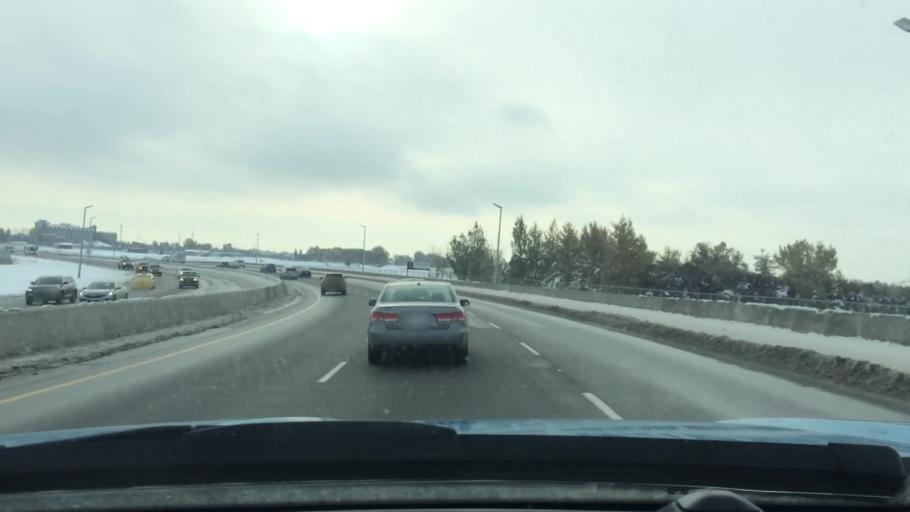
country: CA
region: Alberta
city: Calgary
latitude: 51.0935
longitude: -114.0255
